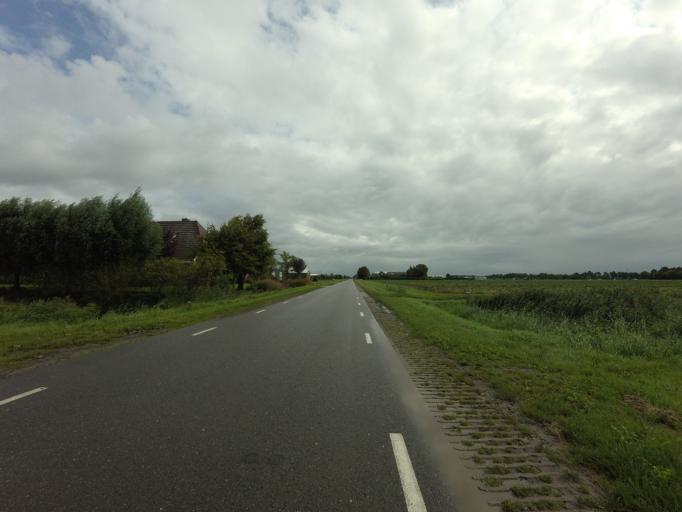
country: NL
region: North Holland
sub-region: Gemeente Medemblik
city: Medemblik
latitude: 52.7018
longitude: 5.1727
